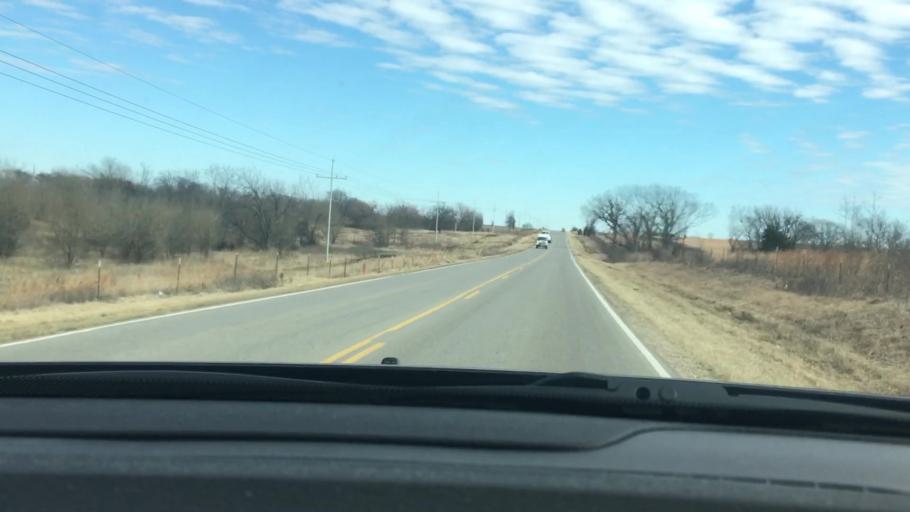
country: US
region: Oklahoma
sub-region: Garvin County
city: Stratford
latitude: 34.7967
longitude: -96.9233
